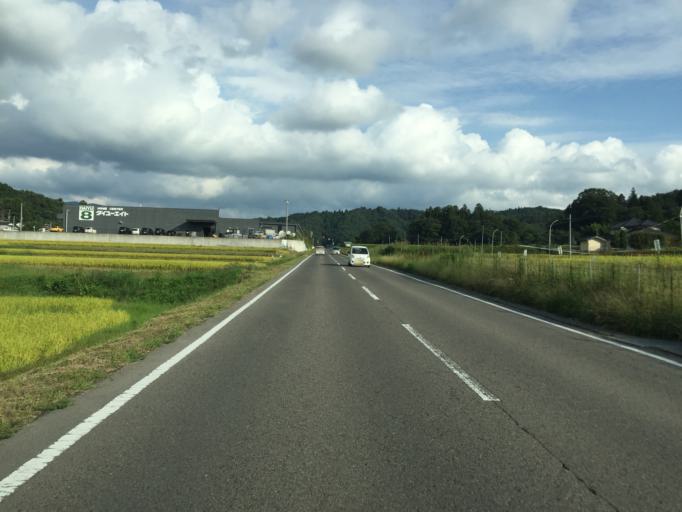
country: JP
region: Fukushima
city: Fukushima-shi
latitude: 37.6694
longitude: 140.5706
